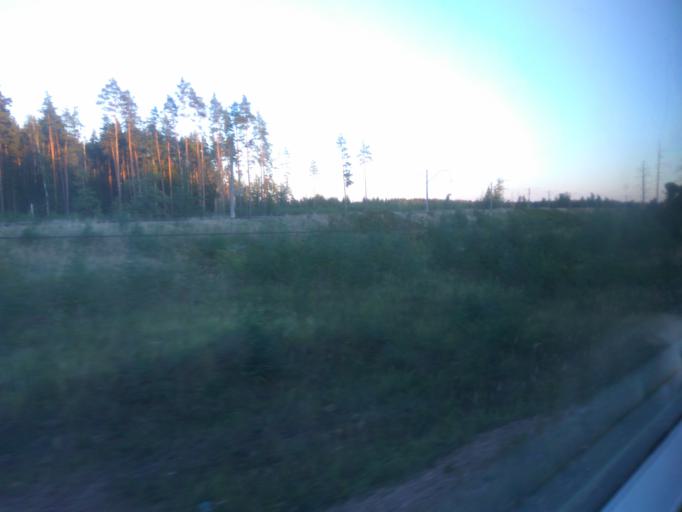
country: RU
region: Moskovskaya
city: Fryazevo
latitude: 55.7420
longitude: 38.4796
